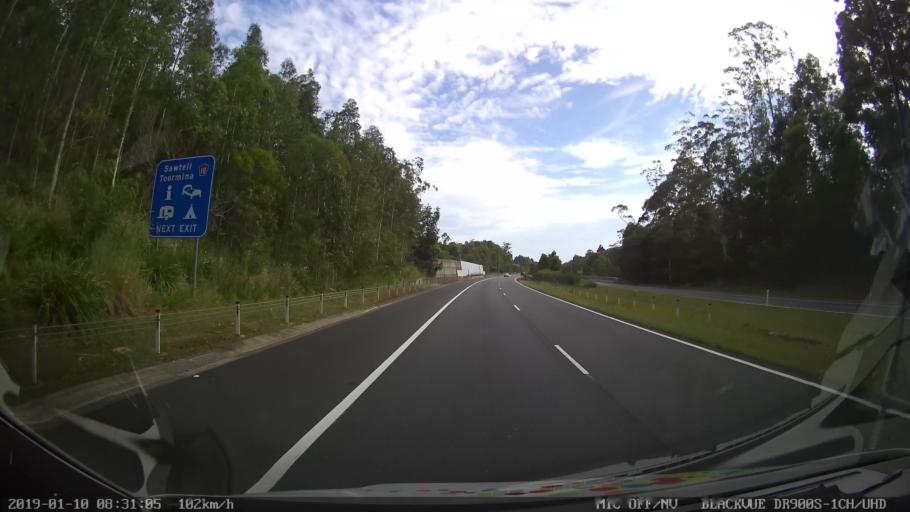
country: AU
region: New South Wales
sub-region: Coffs Harbour
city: Bonville
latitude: -30.3611
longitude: 153.0570
